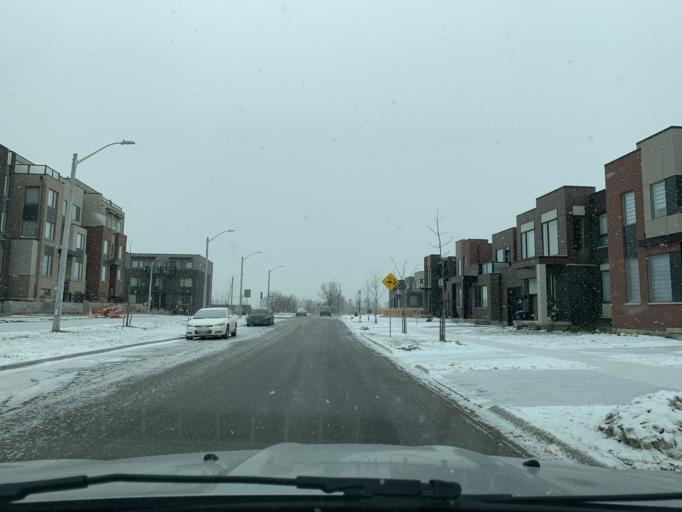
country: CA
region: Ontario
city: Concord
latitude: 43.7333
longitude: -79.4779
